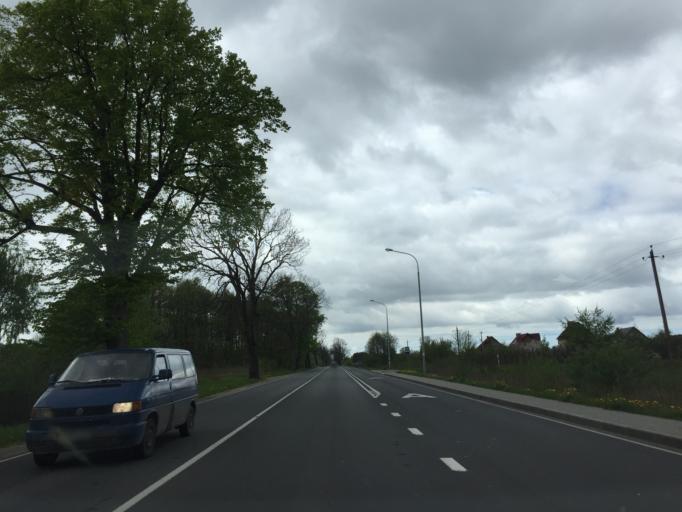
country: RU
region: Kaliningrad
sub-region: Gorod Kaliningrad
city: Kaliningrad
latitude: 54.6594
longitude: 20.3982
